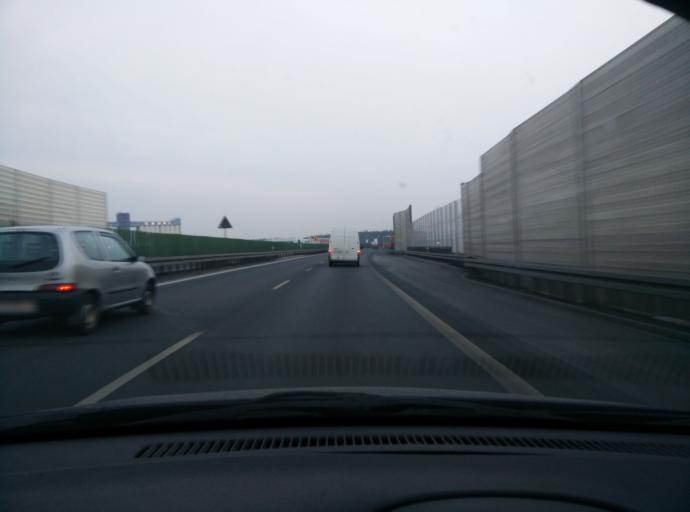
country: PL
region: Greater Poland Voivodeship
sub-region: Powiat poznanski
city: Kornik
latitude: 52.3119
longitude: 17.0458
